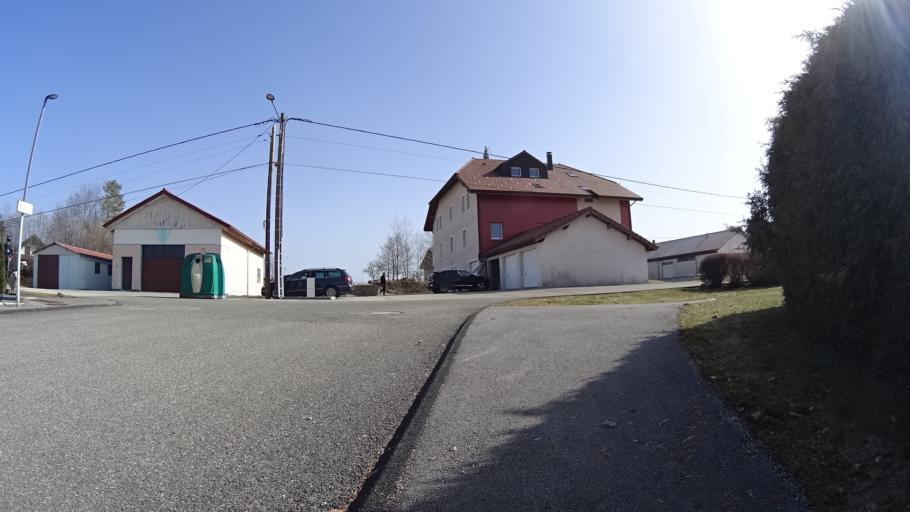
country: FR
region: Franche-Comte
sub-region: Departement du Doubs
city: Frasne
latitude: 46.8520
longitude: 6.1488
